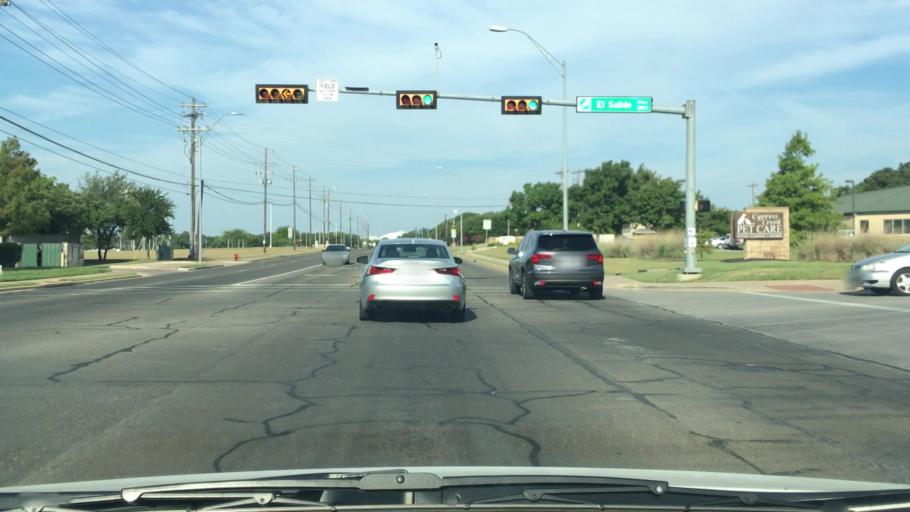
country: US
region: Texas
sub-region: Williamson County
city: Cedar Park
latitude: 30.4751
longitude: -97.8412
